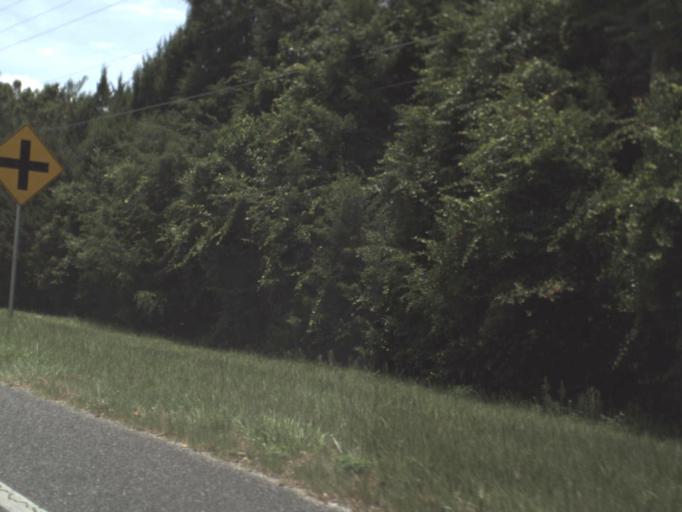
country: US
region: Florida
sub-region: Dixie County
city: Cross City
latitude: 29.6109
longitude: -83.0868
